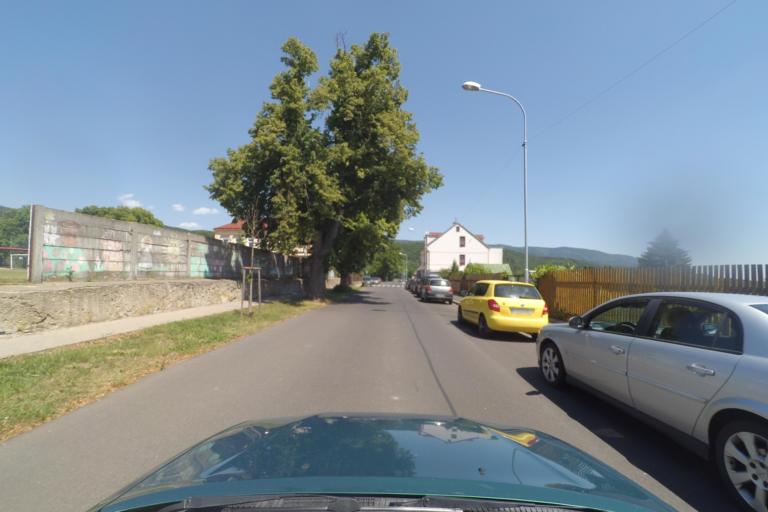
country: CZ
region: Ustecky
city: Novosedlice
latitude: 50.6726
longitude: 13.8063
